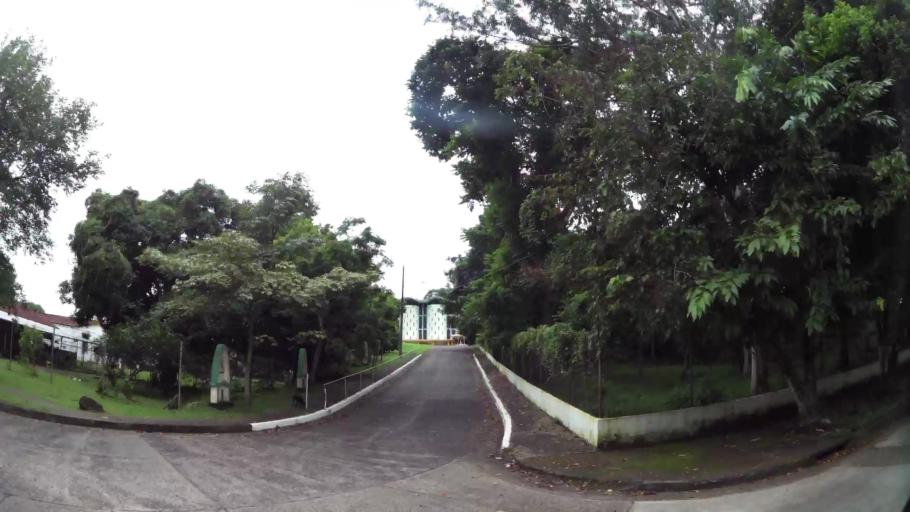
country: PA
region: Panama
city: Panama
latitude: 9.0227
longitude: -79.5201
